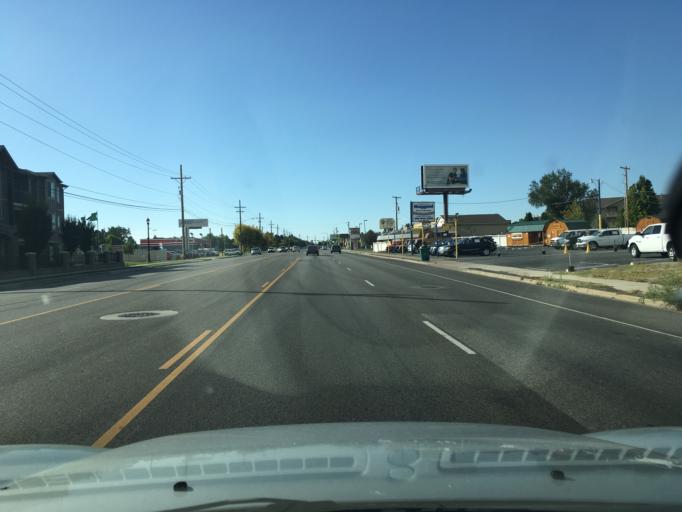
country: US
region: Utah
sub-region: Davis County
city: Layton
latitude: 41.0812
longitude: -111.9909
